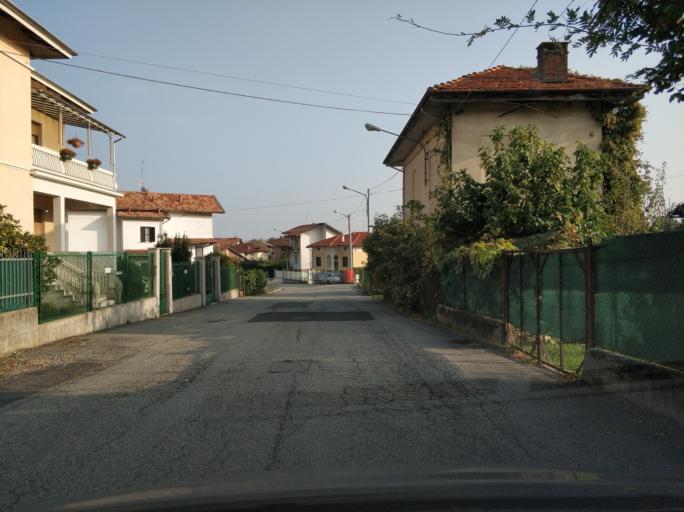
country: IT
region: Piedmont
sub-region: Provincia di Biella
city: Ronco Biellese
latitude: 45.5746
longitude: 8.0725
